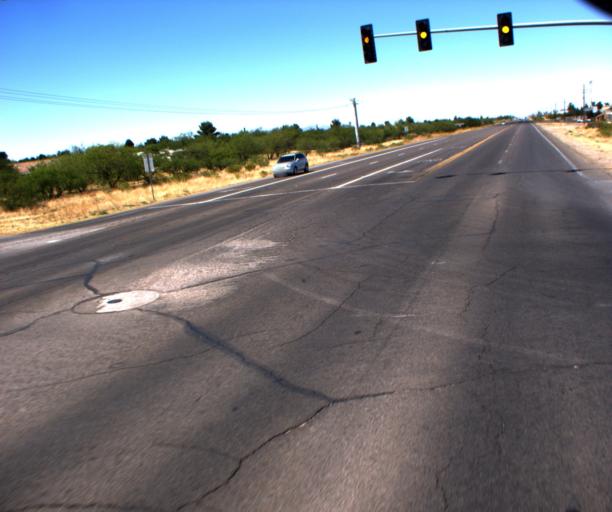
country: US
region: Arizona
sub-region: Cochise County
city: Sierra Vista Southeast
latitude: 31.4672
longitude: -110.2574
